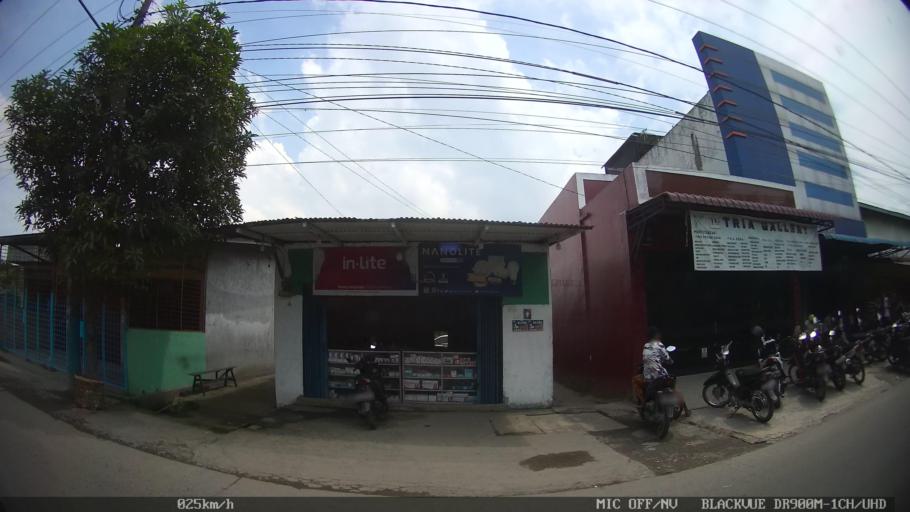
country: ID
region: North Sumatra
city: Labuhan Deli
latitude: 3.6571
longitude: 98.6713
